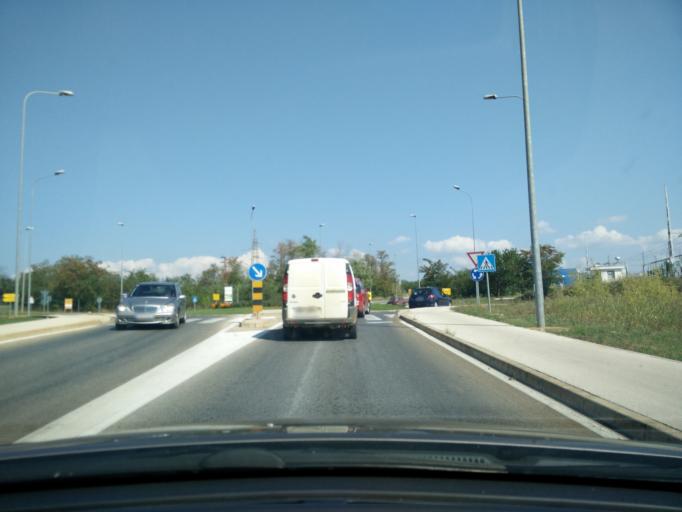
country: HR
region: Istarska
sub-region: Grad Porec
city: Porec
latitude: 45.2593
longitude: 13.6300
